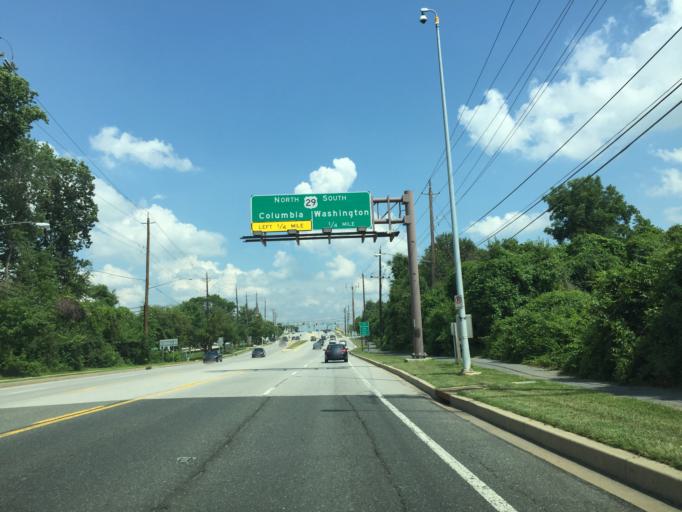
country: US
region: Maryland
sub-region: Montgomery County
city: Fairland
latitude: 39.0642
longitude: -76.9686
